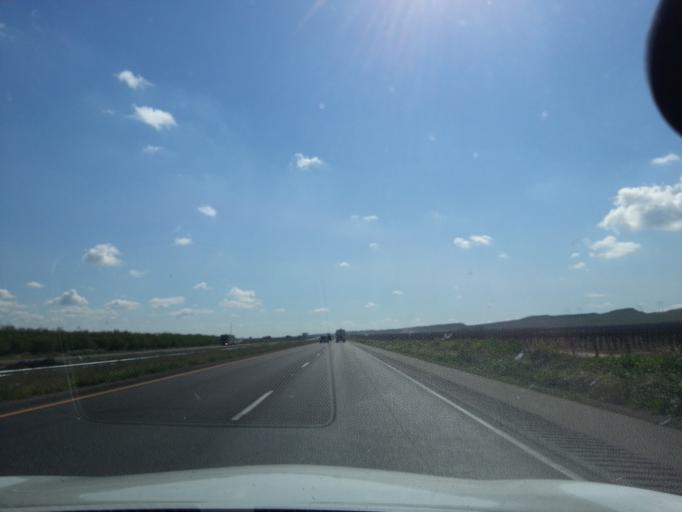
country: US
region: California
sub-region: Fresno County
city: Coalinga
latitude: 36.3628
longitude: -120.3292
